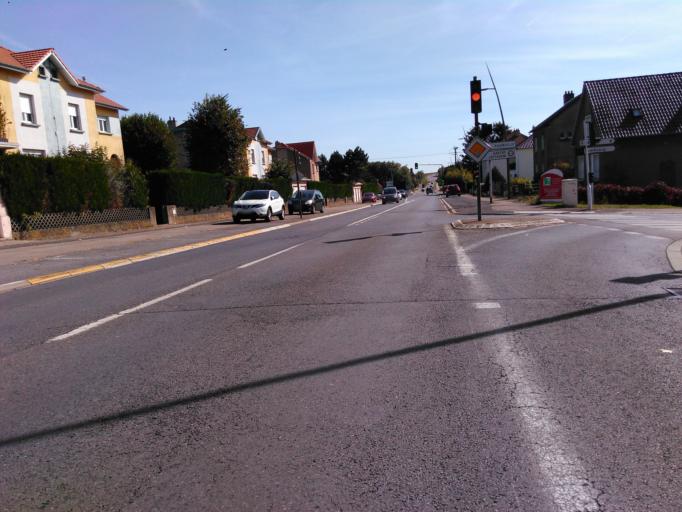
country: FR
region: Lorraine
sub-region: Departement de la Moselle
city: Hettange-Grande
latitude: 49.3987
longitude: 6.1618
